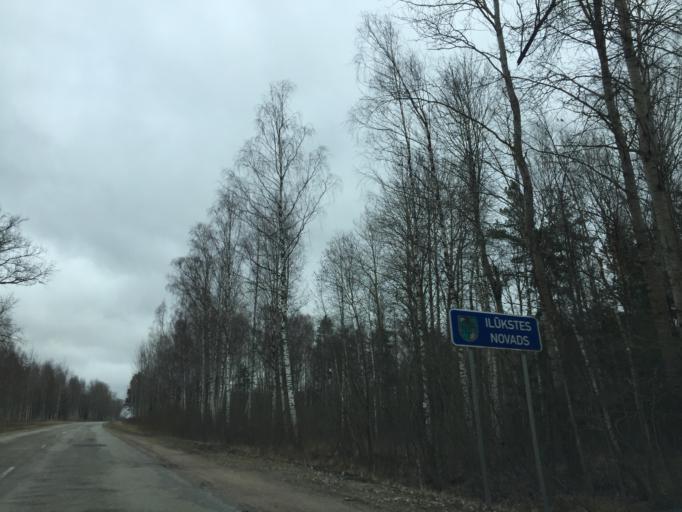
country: LV
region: Ilukste
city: Ilukste
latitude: 55.9655
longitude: 26.3041
